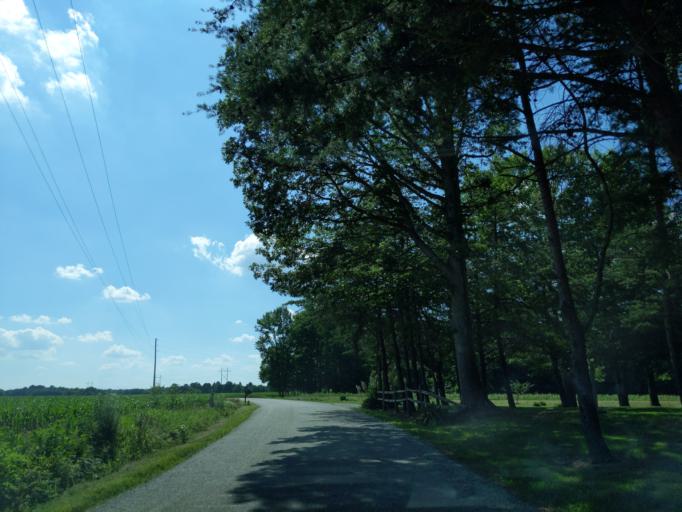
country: US
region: Indiana
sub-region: Ripley County
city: Osgood
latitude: 39.1896
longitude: -85.4151
